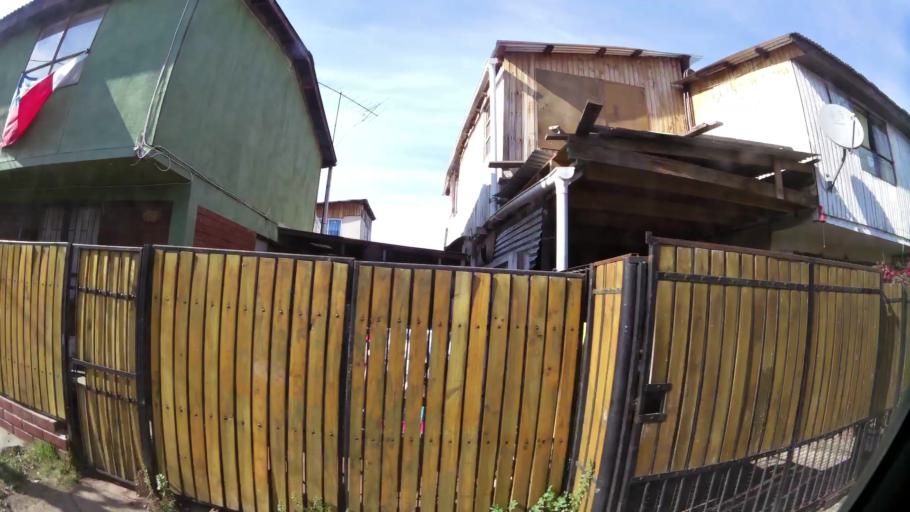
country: CL
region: Santiago Metropolitan
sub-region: Provincia de Talagante
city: Talagante
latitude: -33.6747
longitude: -70.9440
